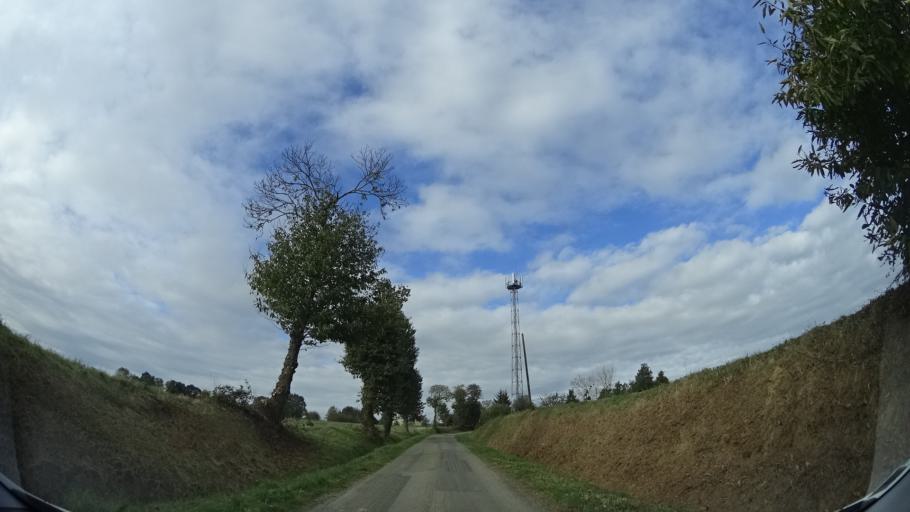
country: FR
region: Brittany
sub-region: Departement d'Ille-et-Vilaine
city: Vignoc
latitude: 48.2408
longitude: -1.8005
